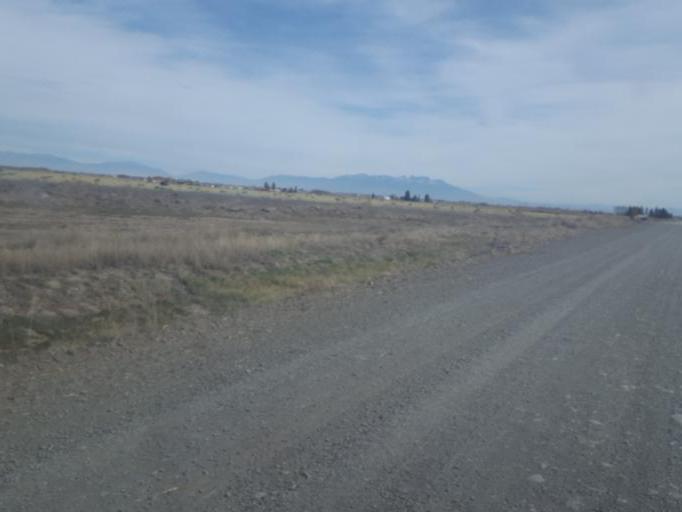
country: US
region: Colorado
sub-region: Rio Grande County
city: Monte Vista
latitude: 37.4011
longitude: -106.0887
